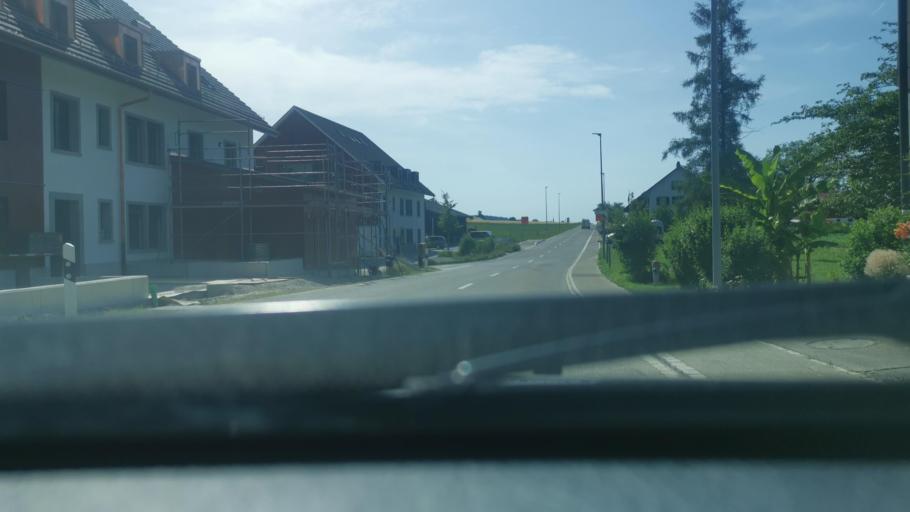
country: CH
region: Zurich
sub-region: Bezirk Winterthur
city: Sulz
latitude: 47.5686
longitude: 8.8017
